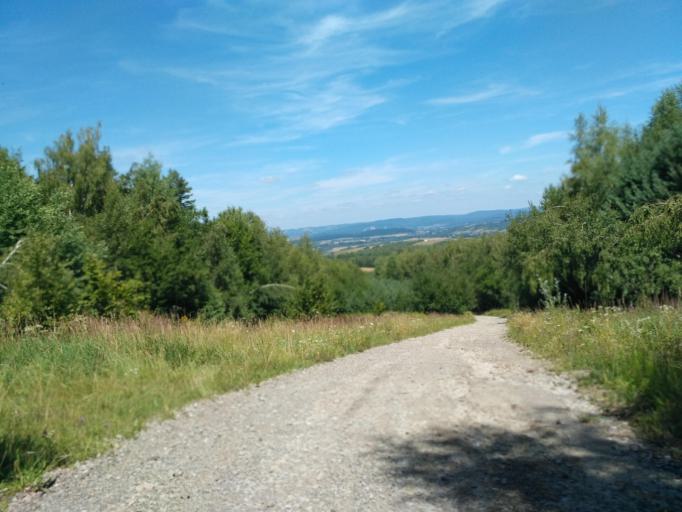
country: PL
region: Subcarpathian Voivodeship
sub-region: Powiat sanocki
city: Bukowsko
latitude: 49.4907
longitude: 22.0902
